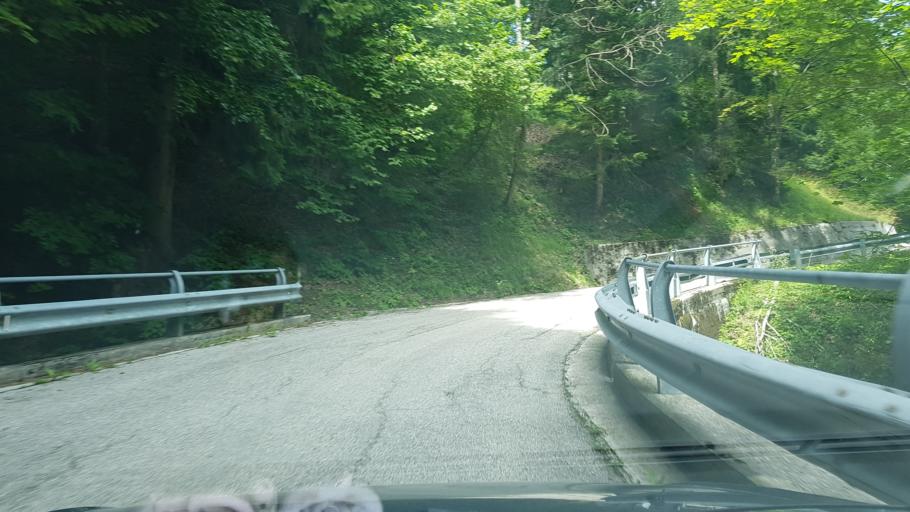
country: IT
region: Friuli Venezia Giulia
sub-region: Provincia di Udine
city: Pontebba
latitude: 46.5043
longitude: 13.2510
